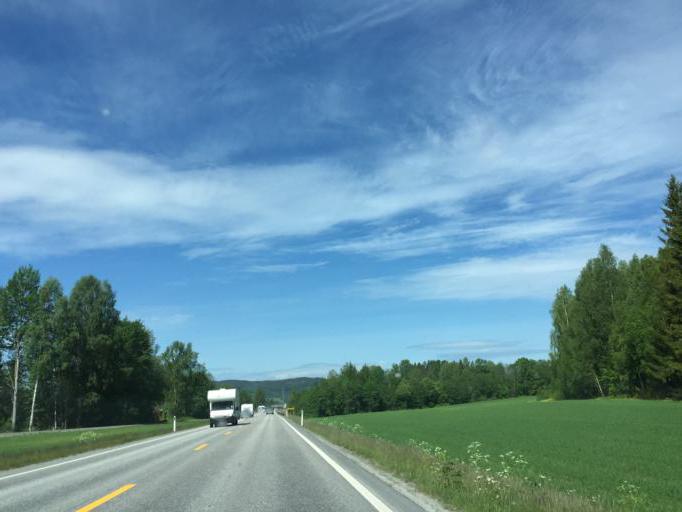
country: NO
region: Hedmark
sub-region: Sor-Odal
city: Skarnes
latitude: 60.2550
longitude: 11.7029
